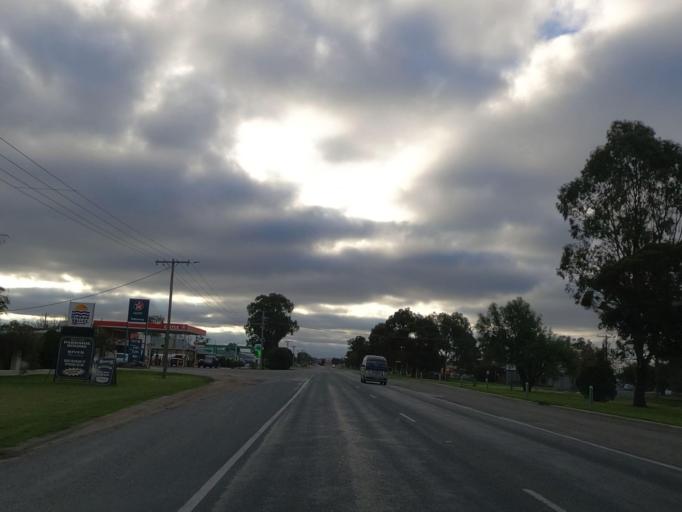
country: AU
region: Victoria
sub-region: Swan Hill
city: Swan Hill
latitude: -35.7404
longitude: 143.9196
